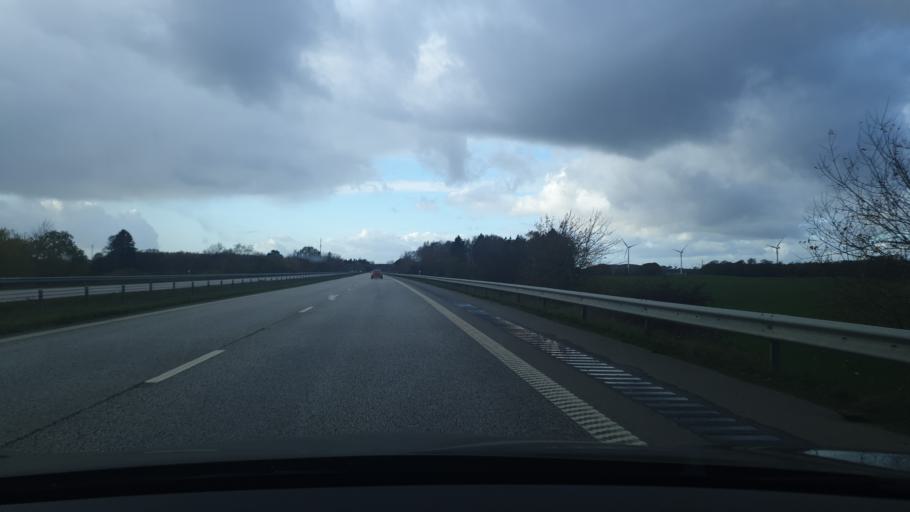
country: SE
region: Skane
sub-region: Svedala Kommun
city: Svedala
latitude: 55.5264
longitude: 13.2149
